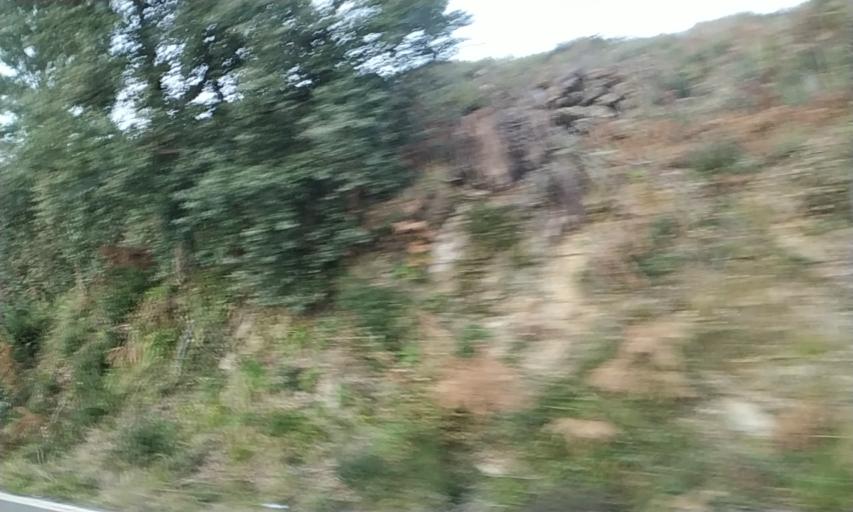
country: PT
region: Vila Real
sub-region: Mondim de Basto
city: Mondim de Basto
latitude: 41.4611
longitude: -7.9588
